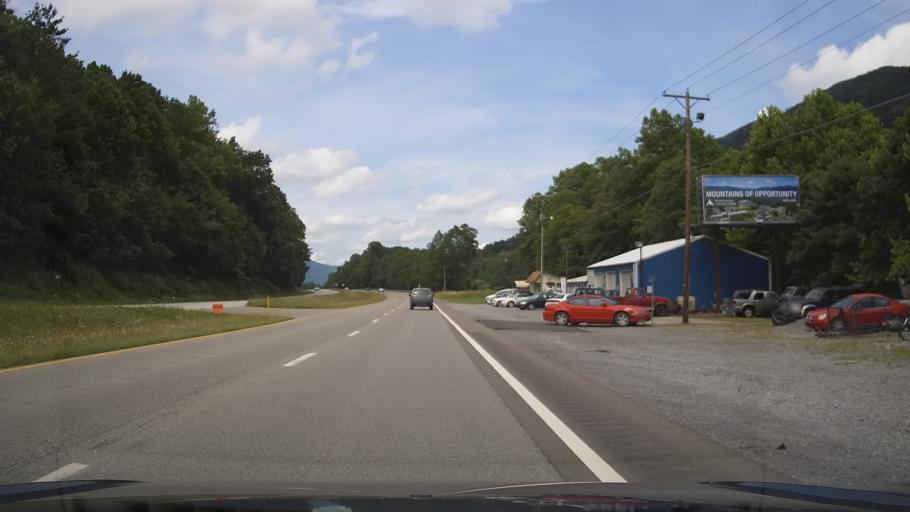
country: US
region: Virginia
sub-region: Wise County
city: Big Stone Gap
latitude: 36.8214
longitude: -82.7761
